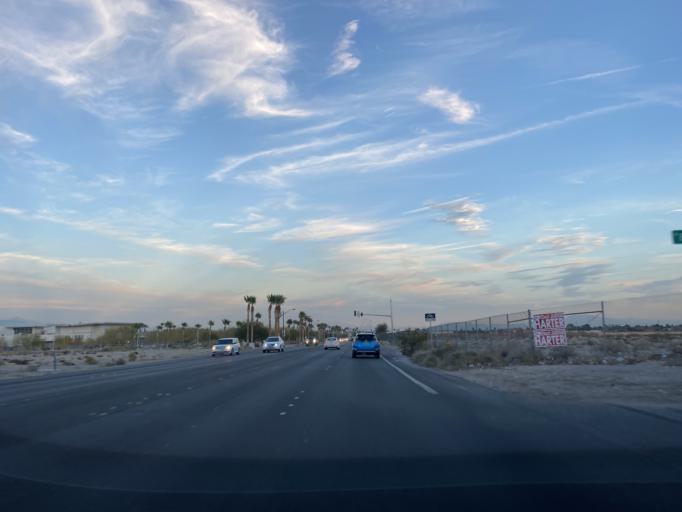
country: US
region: Nevada
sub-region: Clark County
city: Summerlin South
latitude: 36.2702
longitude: -115.2766
